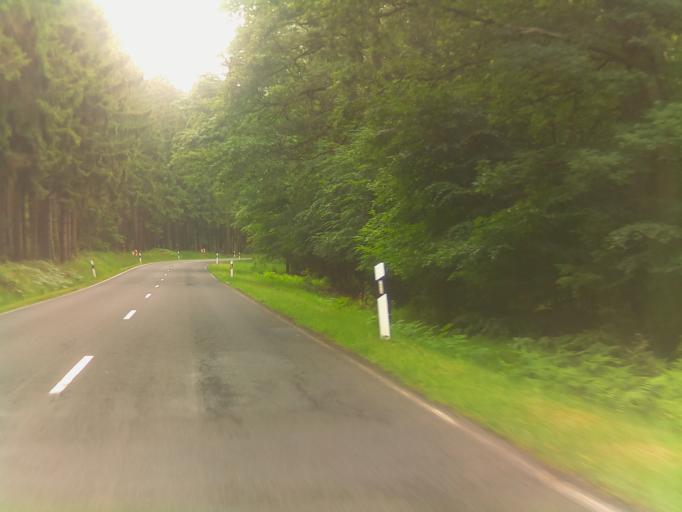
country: DE
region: Hesse
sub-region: Regierungsbezirk Darmstadt
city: Bad Orb
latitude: 50.1874
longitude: 9.4215
